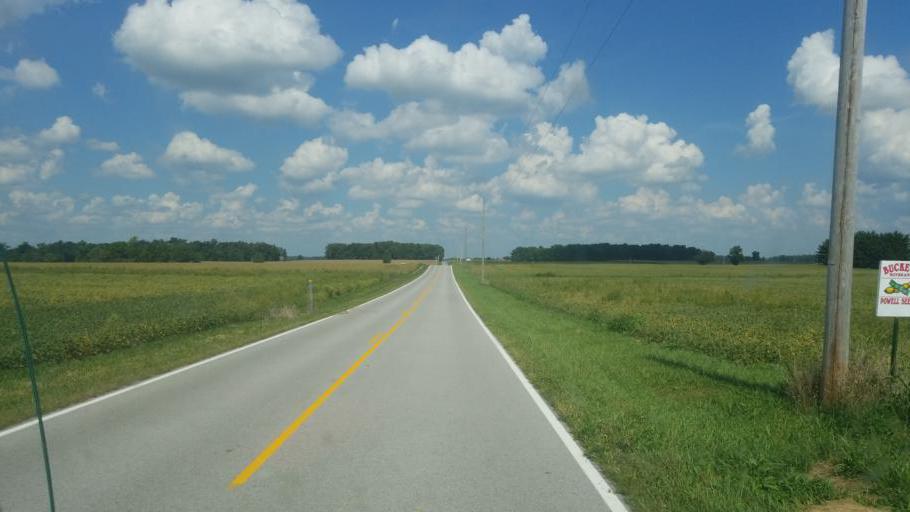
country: US
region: Ohio
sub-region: Hancock County
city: Arlington
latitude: 40.8582
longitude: -83.7275
